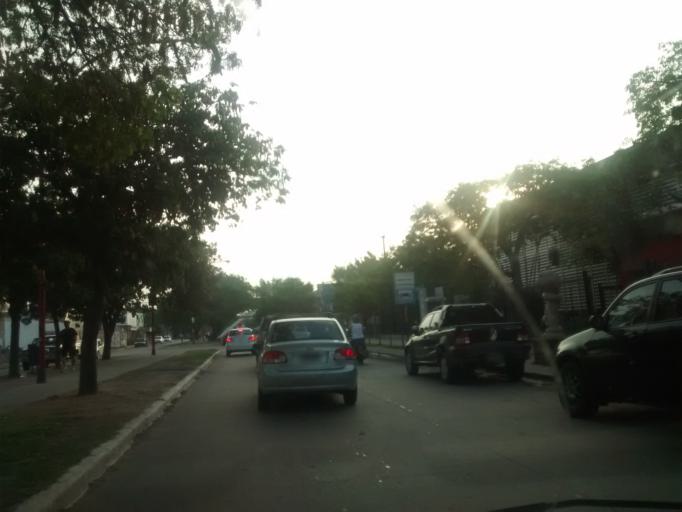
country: AR
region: Chaco
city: Resistencia
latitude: -27.4364
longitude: -58.9701
